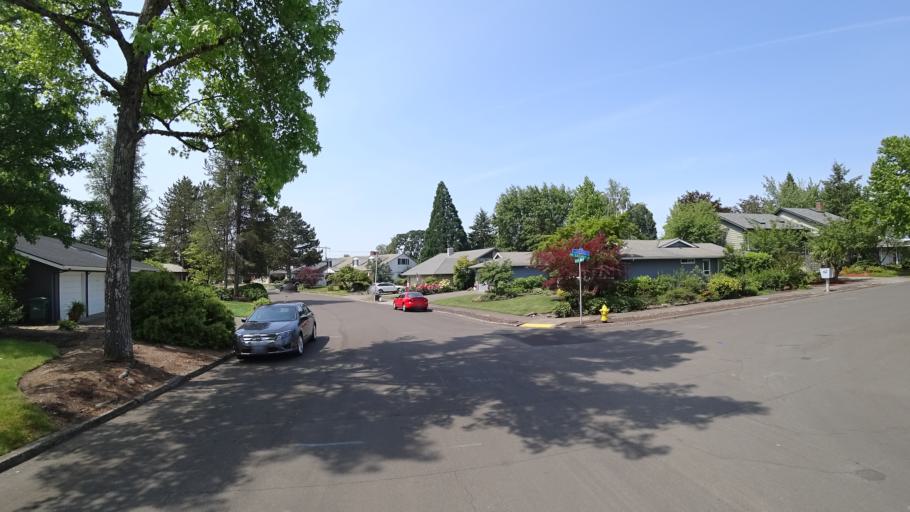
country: US
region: Oregon
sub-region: Washington County
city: Oak Hills
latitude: 45.5407
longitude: -122.8263
